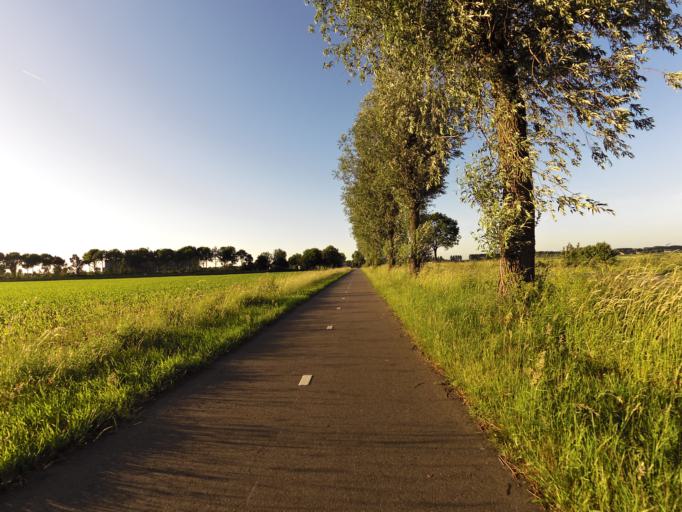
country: NL
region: Gelderland
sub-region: Gemeente Zevenaar
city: Zevenaar
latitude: 51.9612
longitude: 6.0842
